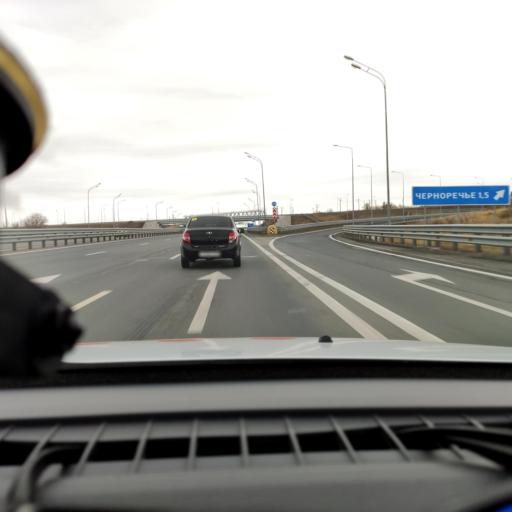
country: RU
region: Samara
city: Smyshlyayevka
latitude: 53.1490
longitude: 50.3774
